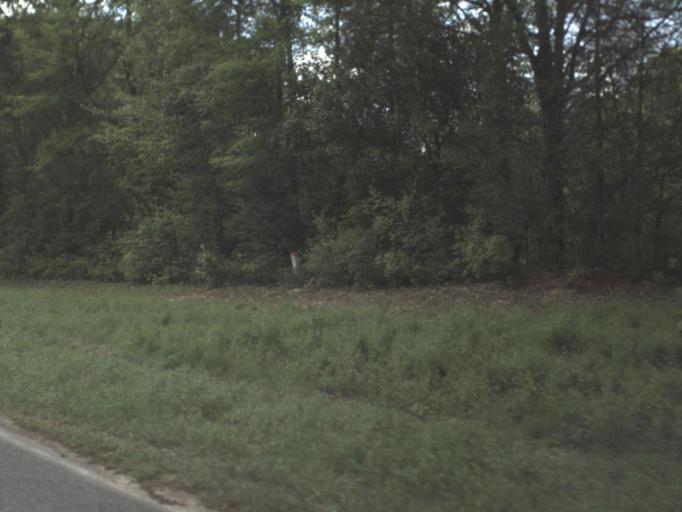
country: US
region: Florida
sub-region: Okaloosa County
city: Crestview
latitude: 30.9230
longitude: -86.6368
